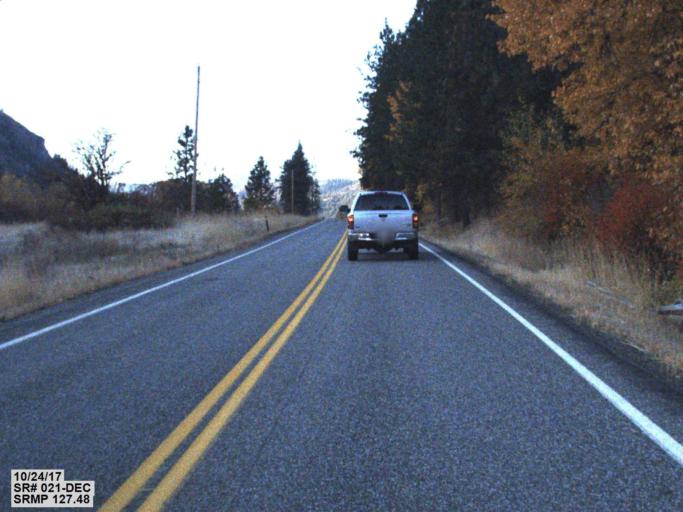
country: US
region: Washington
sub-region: Okanogan County
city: Coulee Dam
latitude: 48.2261
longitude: -118.7048
